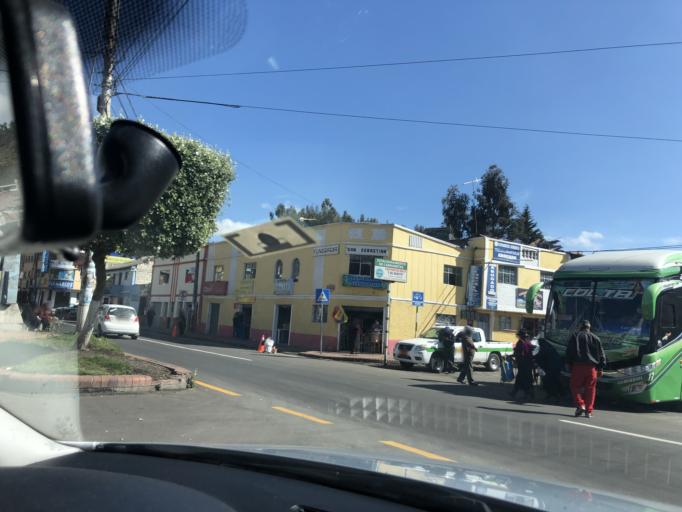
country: EC
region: Chimborazo
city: Riobamba
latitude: -1.7006
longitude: -78.7710
